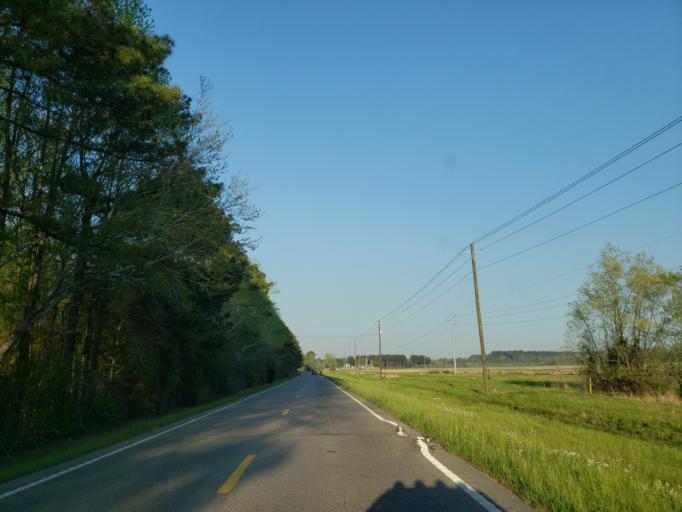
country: US
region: Mississippi
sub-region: Lauderdale County
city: Marion
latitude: 32.3943
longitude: -88.6272
